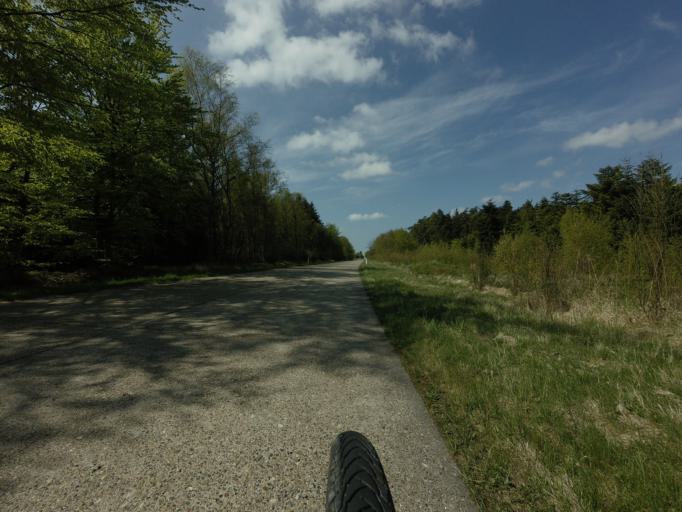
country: DK
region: North Denmark
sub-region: Jammerbugt Kommune
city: Brovst
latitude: 57.1650
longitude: 9.4816
